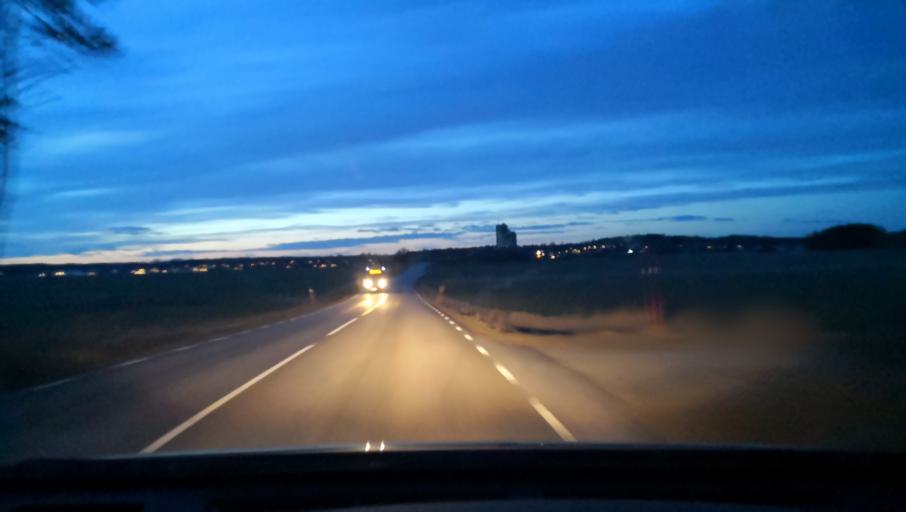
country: SE
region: Uppsala
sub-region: Enkopings Kommun
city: Grillby
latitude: 59.6150
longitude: 17.2671
